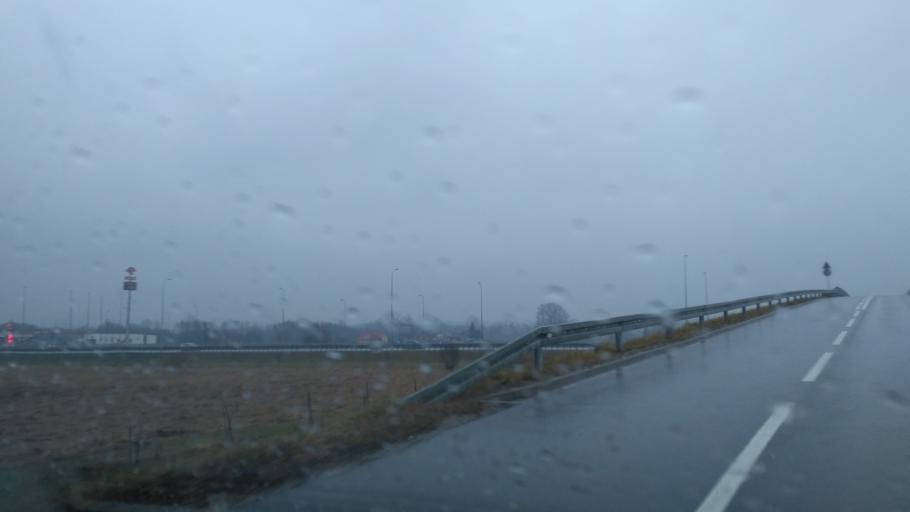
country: PL
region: Subcarpathian Voivodeship
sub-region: Powiat lancucki
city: Czarna
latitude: 50.0913
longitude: 22.1702
